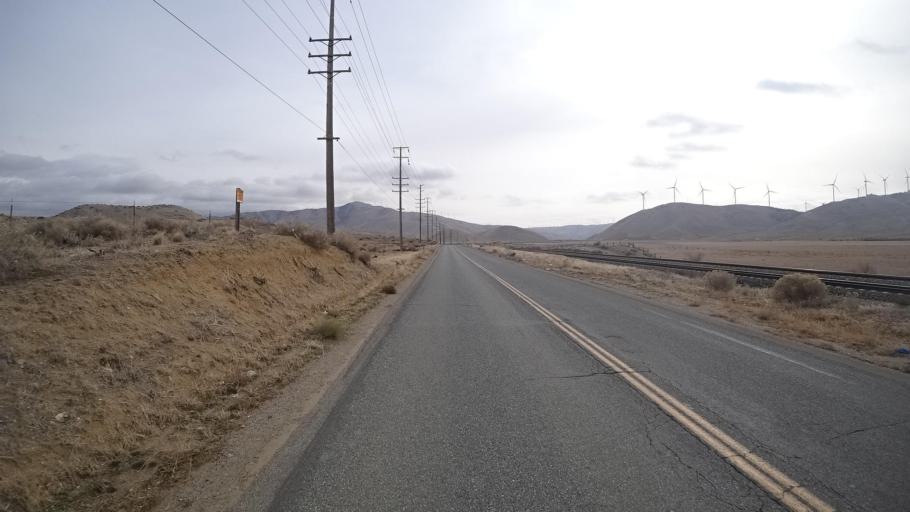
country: US
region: California
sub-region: Kern County
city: Tehachapi
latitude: 35.1210
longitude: -118.3469
